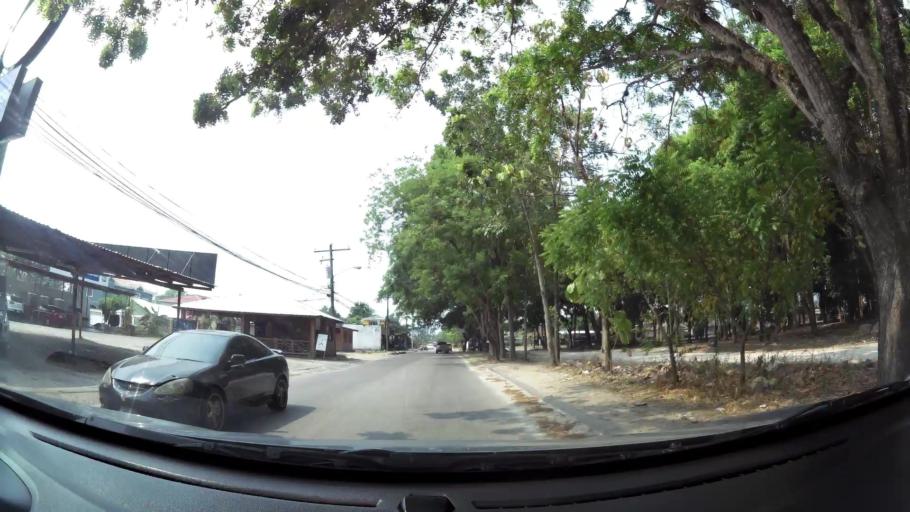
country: HN
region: Cortes
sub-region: San Pedro Sula
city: Pena Blanca
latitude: 15.5441
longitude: -88.0280
